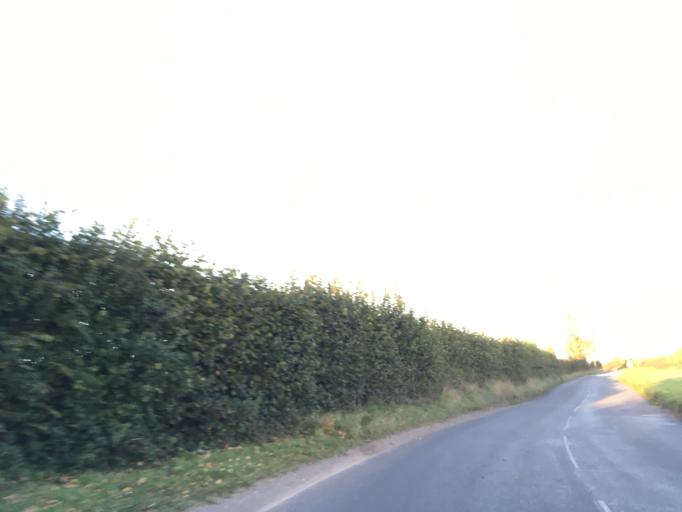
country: GB
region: England
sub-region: South Gloucestershire
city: Alveston
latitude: 51.5862
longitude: -2.5534
